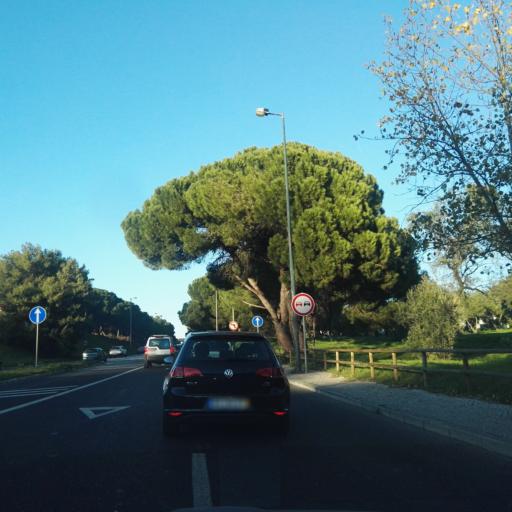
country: PT
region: Lisbon
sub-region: Loures
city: Moscavide
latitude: 38.7720
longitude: -9.1235
